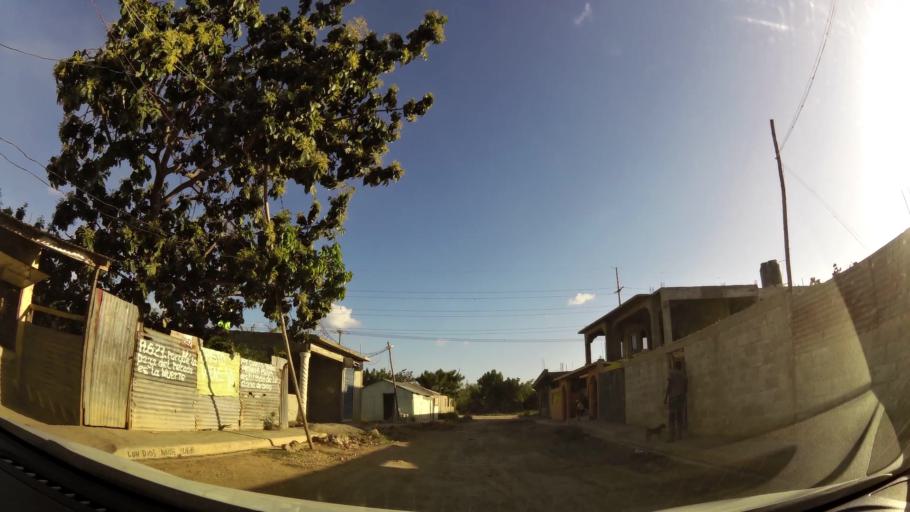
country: DO
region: Santo Domingo
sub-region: Santo Domingo
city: Santo Domingo Este
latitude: 18.4766
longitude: -69.8000
